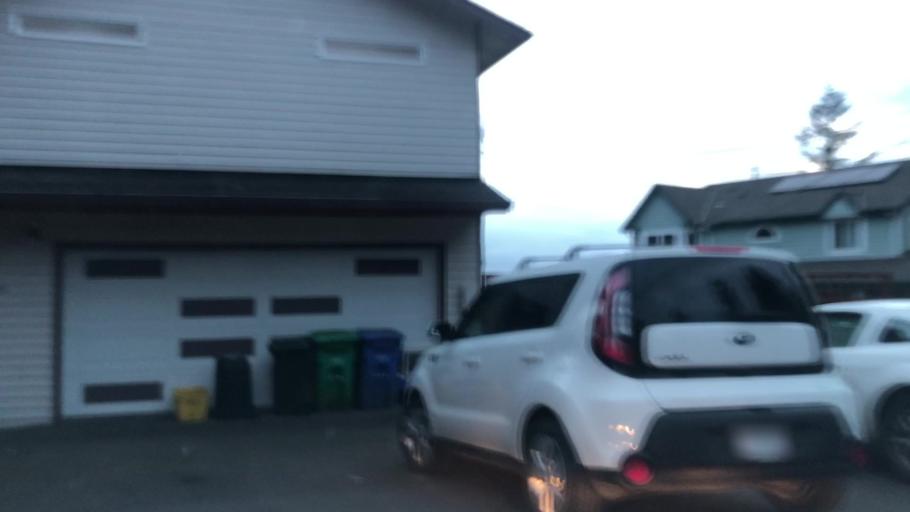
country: US
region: Oregon
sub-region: Multnomah County
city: Portland
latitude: 45.4995
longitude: -122.7149
